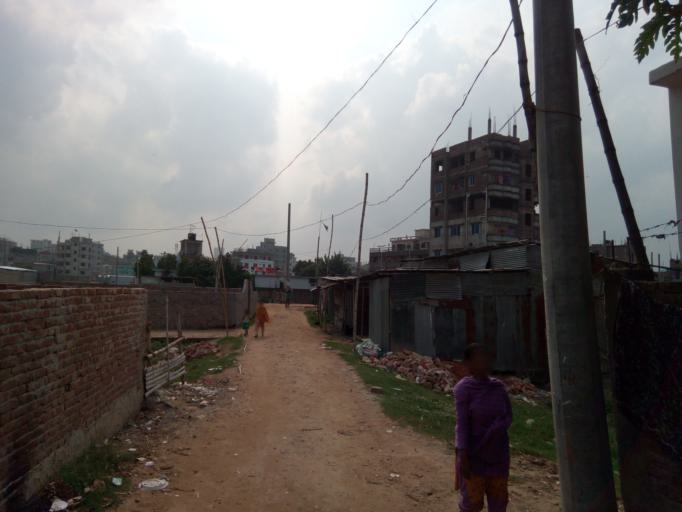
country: BD
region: Dhaka
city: Paltan
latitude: 23.7256
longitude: 90.4403
